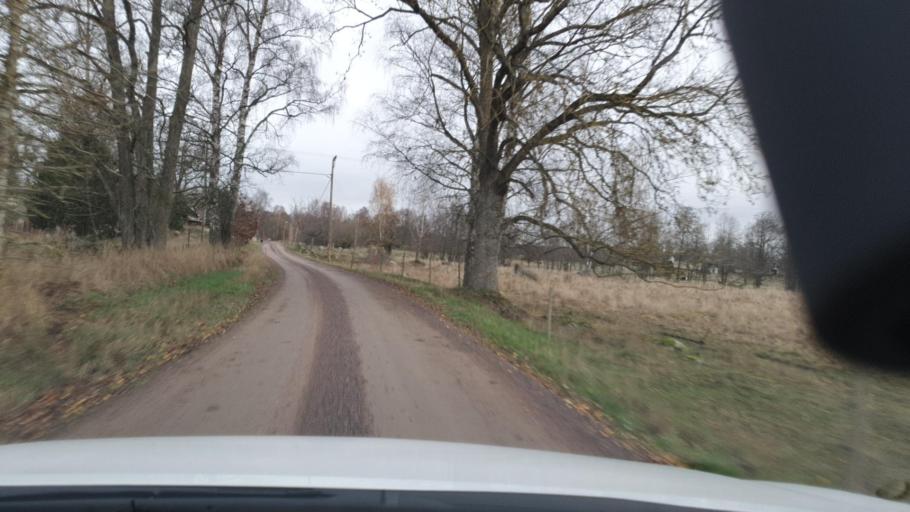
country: SE
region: Kalmar
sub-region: Hultsfreds Kommun
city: Malilla
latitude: 57.3211
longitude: 15.8105
